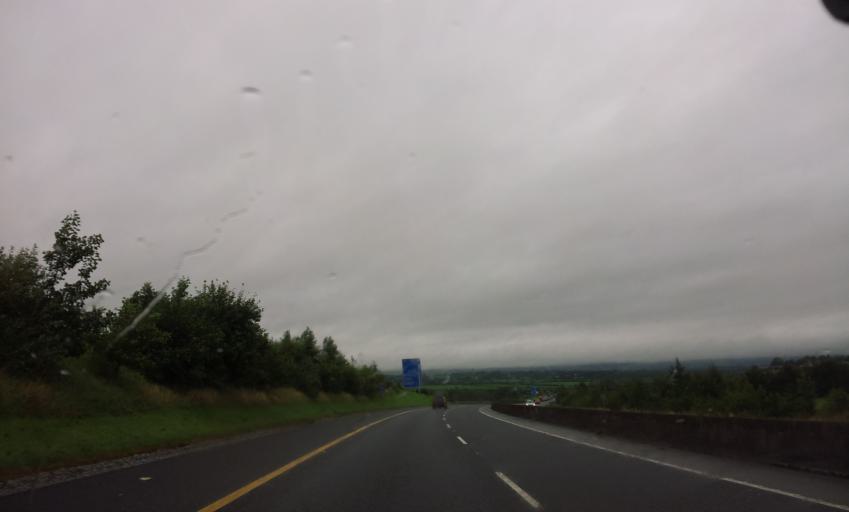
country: IE
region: Munster
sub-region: County Cork
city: Mitchelstown
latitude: 52.2226
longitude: -8.2875
